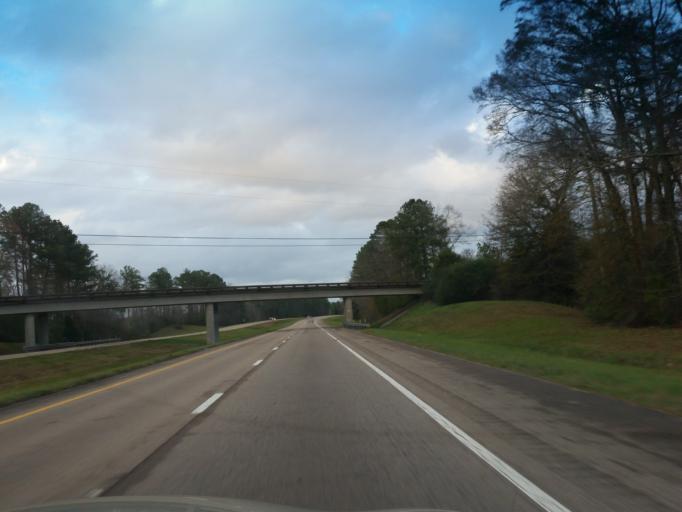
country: US
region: Mississippi
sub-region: Clarke County
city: Stonewall
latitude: 32.0377
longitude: -88.9212
